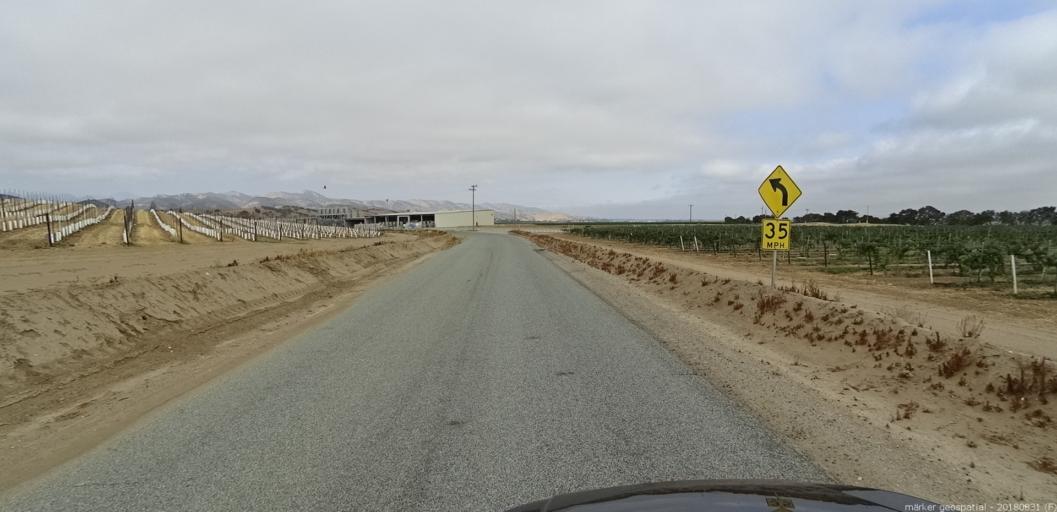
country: US
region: California
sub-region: Monterey County
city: King City
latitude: 36.1710
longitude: -121.1197
